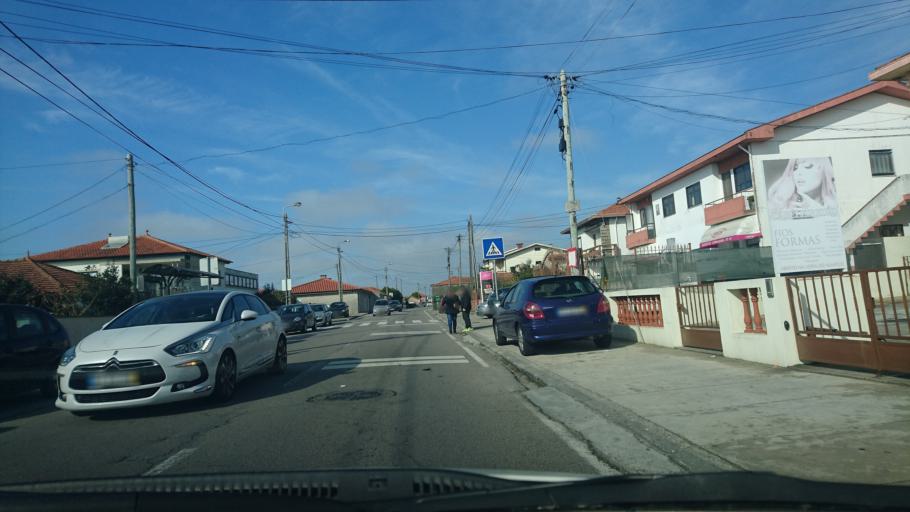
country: PT
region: Aveiro
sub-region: Espinho
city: Souto
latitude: 40.9816
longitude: -8.6320
